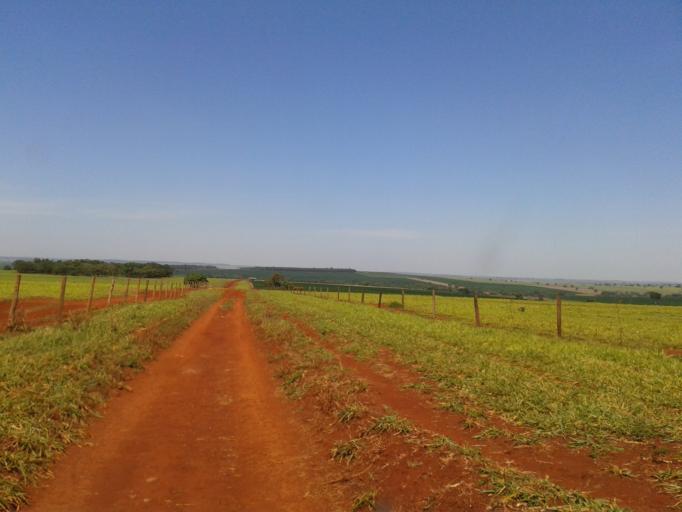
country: BR
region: Minas Gerais
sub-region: Centralina
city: Centralina
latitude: -18.6524
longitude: -49.2721
